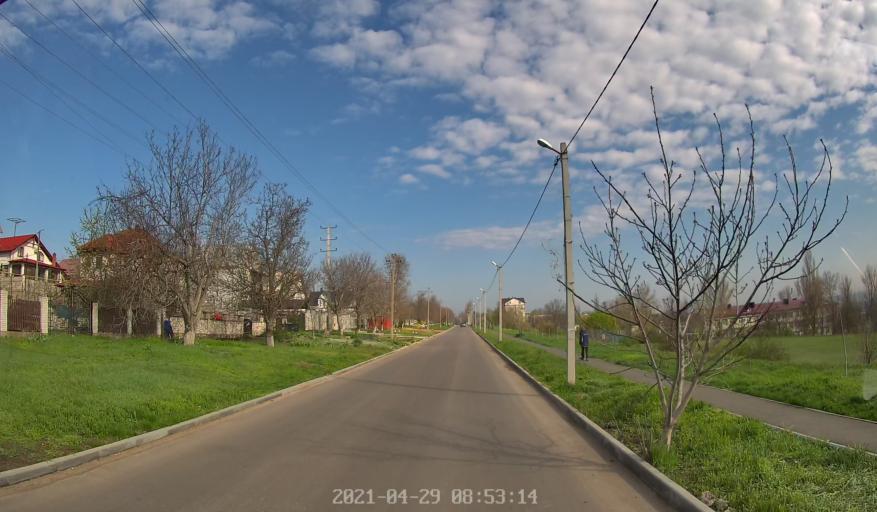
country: MD
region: Chisinau
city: Cricova
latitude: 47.1319
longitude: 28.8612
